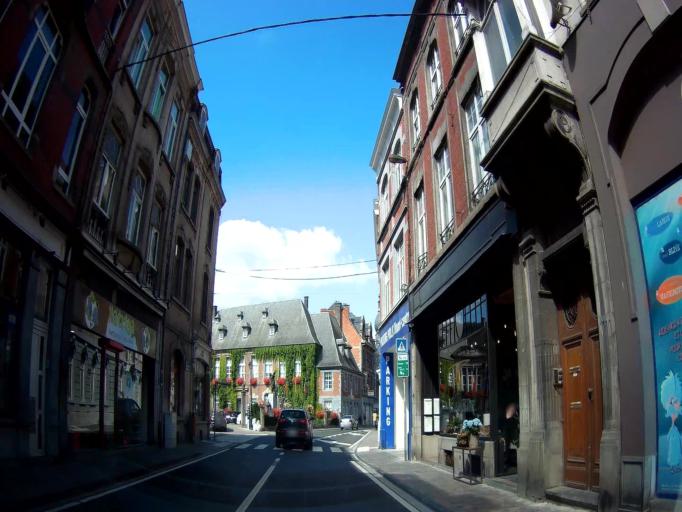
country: BE
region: Wallonia
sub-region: Province de Namur
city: Dinant
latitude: 50.2590
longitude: 4.9137
